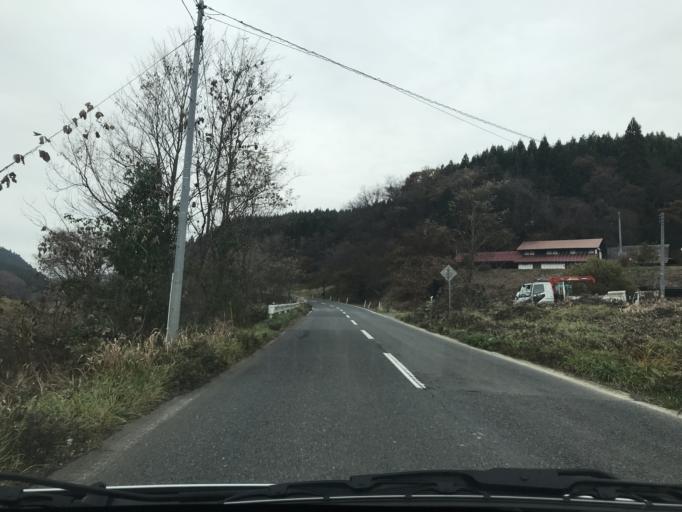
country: JP
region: Iwate
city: Kitakami
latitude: 39.2639
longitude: 141.1829
